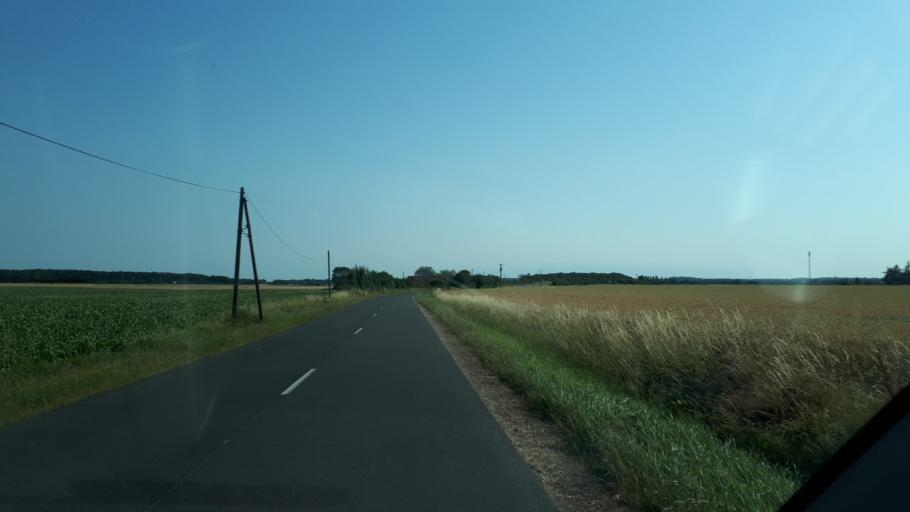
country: FR
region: Centre
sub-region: Departement du Loir-et-Cher
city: Droue
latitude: 48.0111
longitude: 1.0504
